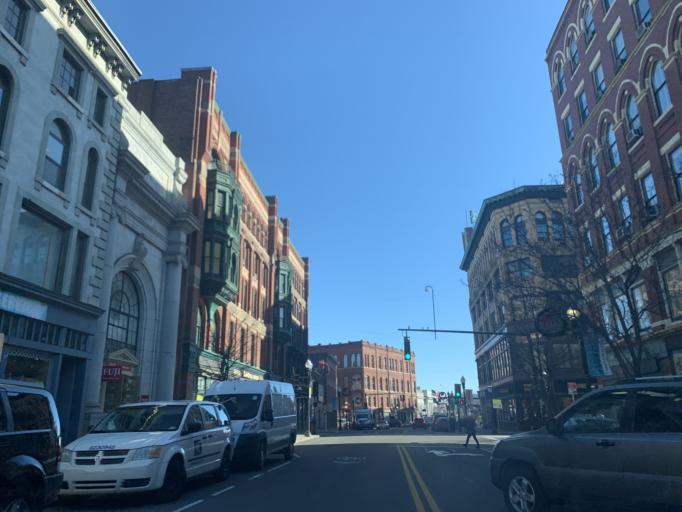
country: US
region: Massachusetts
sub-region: Middlesex County
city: Lowell
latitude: 42.6456
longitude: -71.3090
